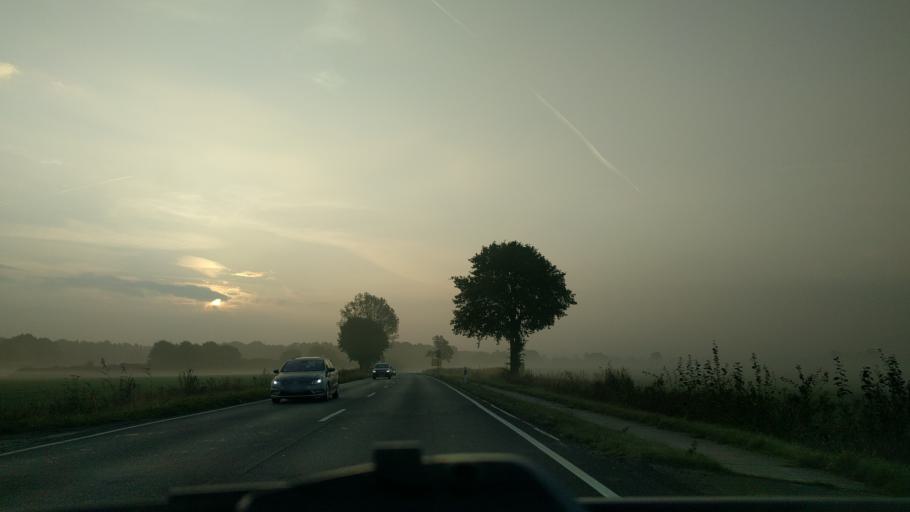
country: DE
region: Lower Saxony
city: Isenbuttel
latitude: 52.4424
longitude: 10.5976
